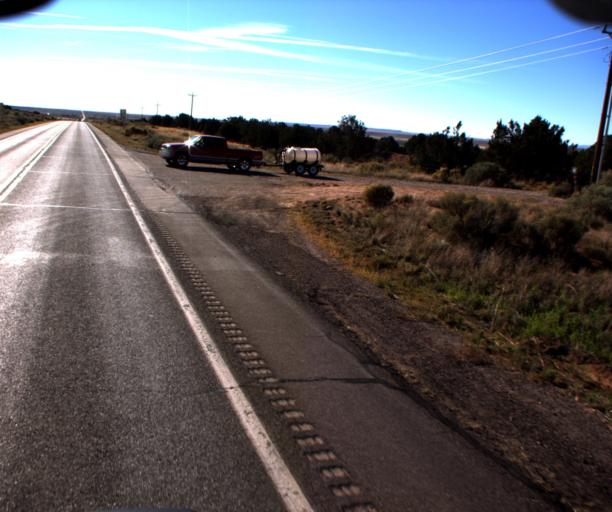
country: US
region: Arizona
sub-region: Mohave County
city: Colorado City
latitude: 36.9597
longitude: -112.9664
